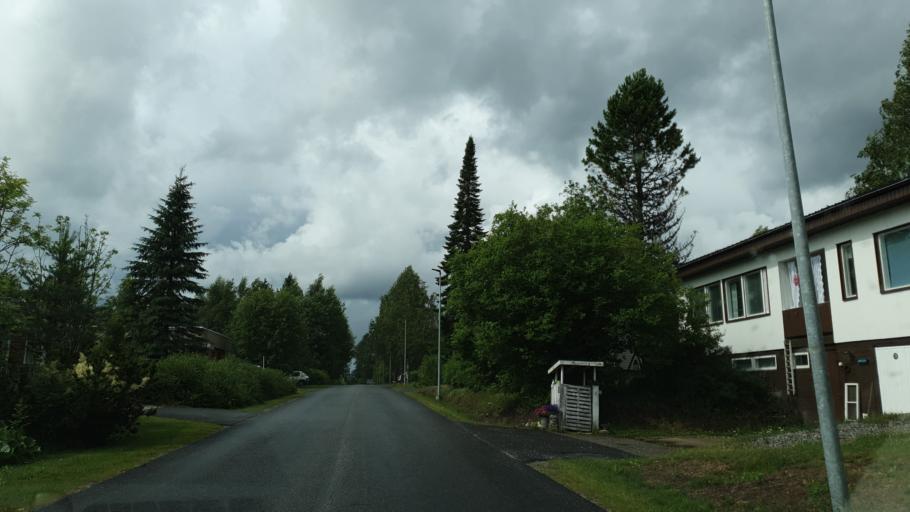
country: FI
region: Kainuu
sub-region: Kehys-Kainuu
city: Kuhmo
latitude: 64.1165
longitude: 29.5055
